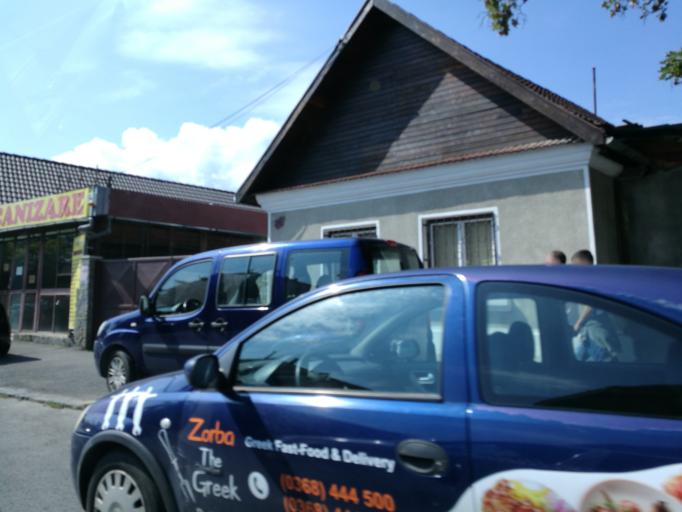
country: RO
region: Brasov
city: Brasov
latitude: 45.6579
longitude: 25.5876
